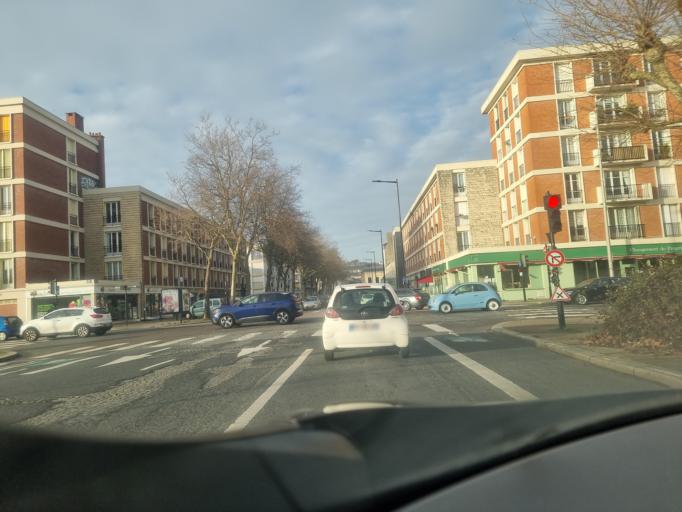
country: FR
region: Haute-Normandie
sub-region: Departement de la Seine-Maritime
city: Le Havre
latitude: 49.4905
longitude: 0.1168
